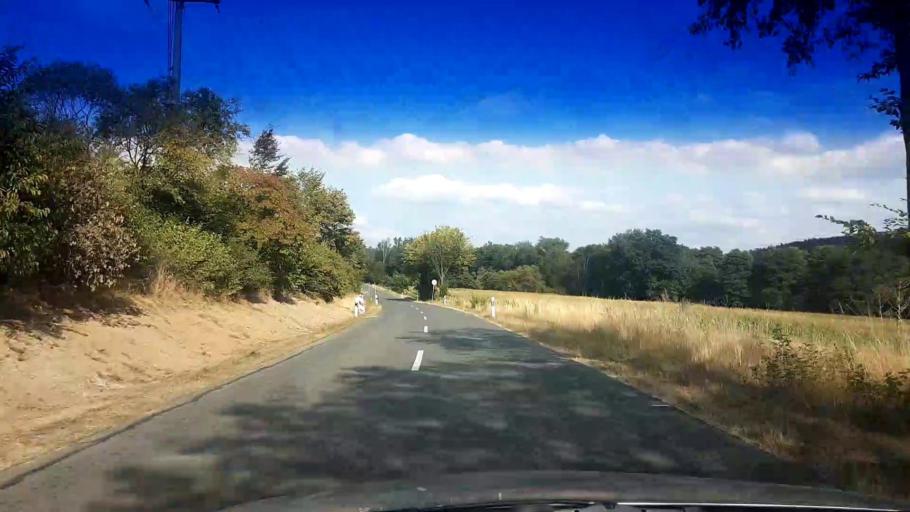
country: DE
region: Bavaria
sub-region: Upper Palatinate
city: Waldsassen
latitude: 50.0238
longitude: 12.3345
